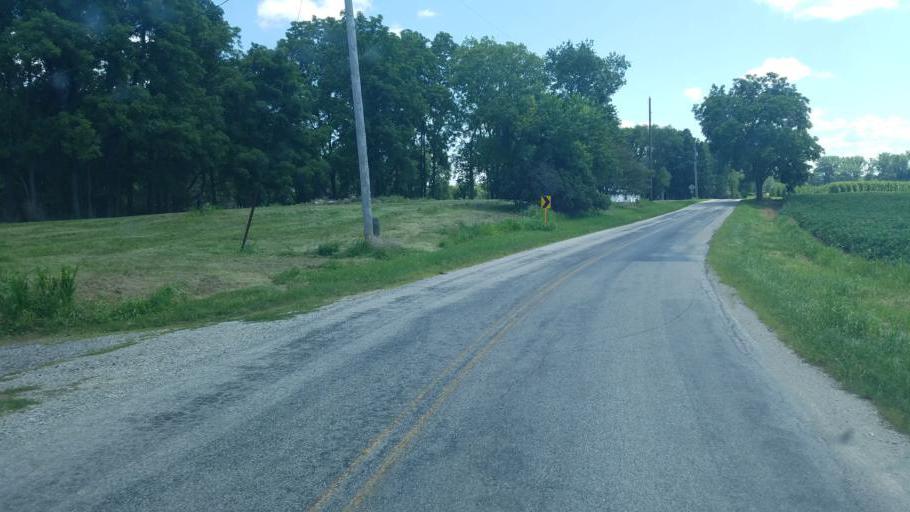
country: US
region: Ohio
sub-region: Marion County
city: Marion
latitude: 40.6292
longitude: -83.1828
